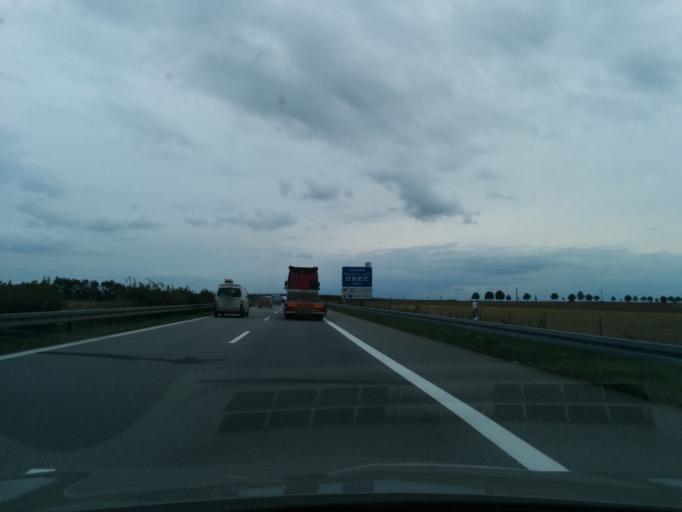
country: DE
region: Mecklenburg-Vorpommern
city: Jarmen
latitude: 53.8660
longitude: 13.3426
